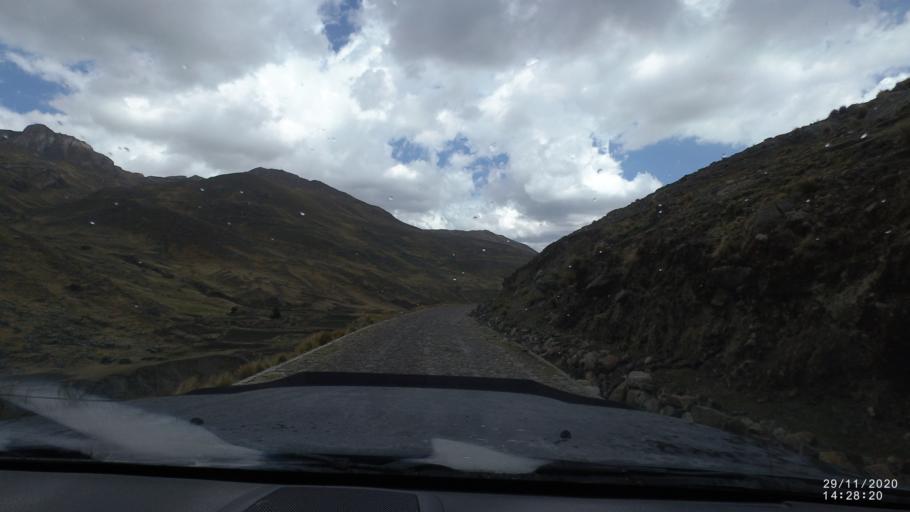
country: BO
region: Cochabamba
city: Sipe Sipe
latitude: -17.2584
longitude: -66.3606
